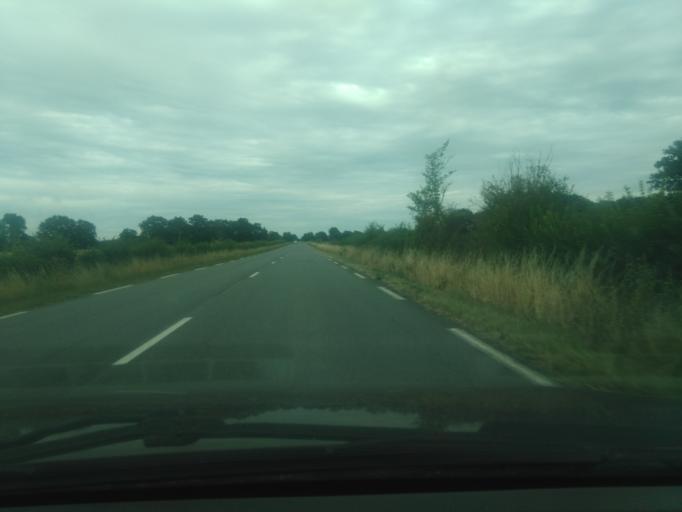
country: FR
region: Centre
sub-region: Departement du Cher
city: Charenton-du-Cher
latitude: 46.7311
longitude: 2.6058
